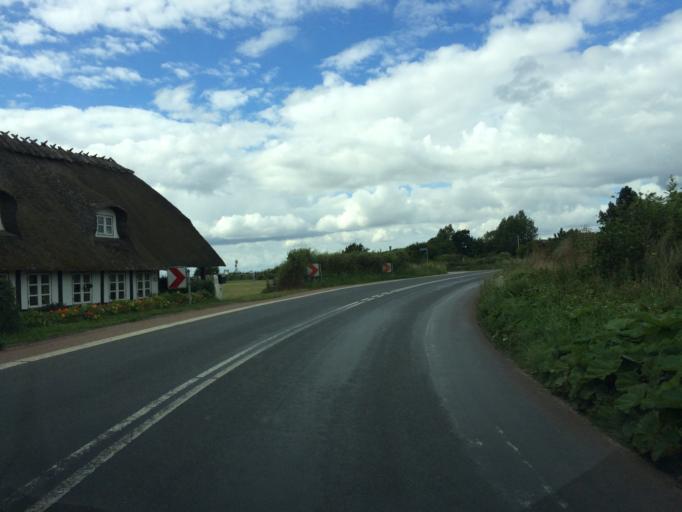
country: DK
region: South Denmark
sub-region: Assens Kommune
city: Harby
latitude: 55.1587
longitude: 10.1409
